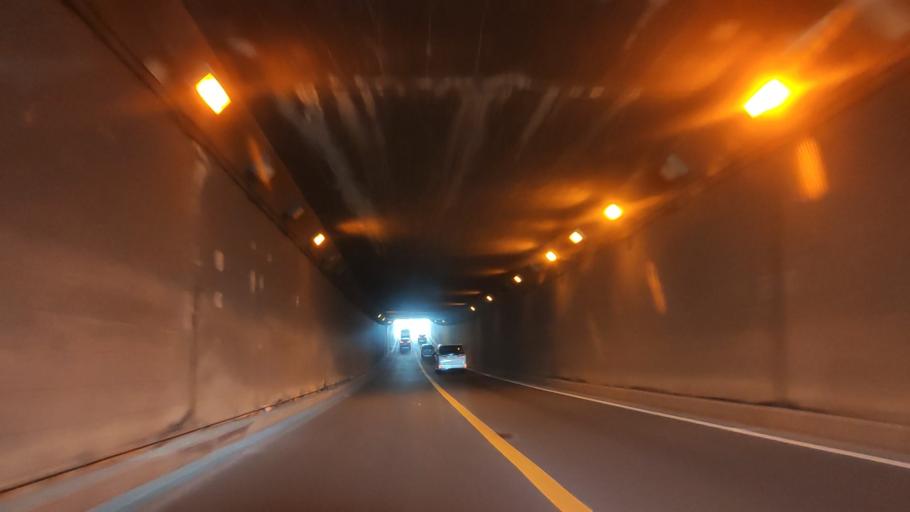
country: JP
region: Osaka
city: Tondabayashicho
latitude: 34.4910
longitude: 135.5842
